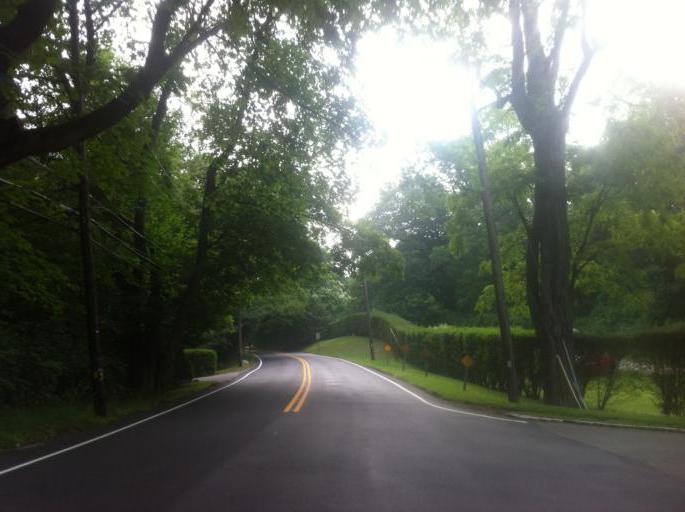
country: US
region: New York
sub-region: Nassau County
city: Locust Valley
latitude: 40.8688
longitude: -73.5699
